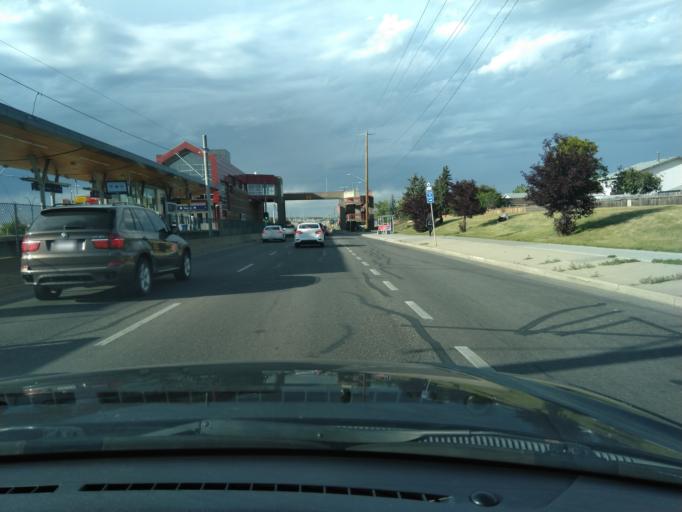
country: CA
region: Alberta
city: Calgary
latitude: 51.0858
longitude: -113.9816
